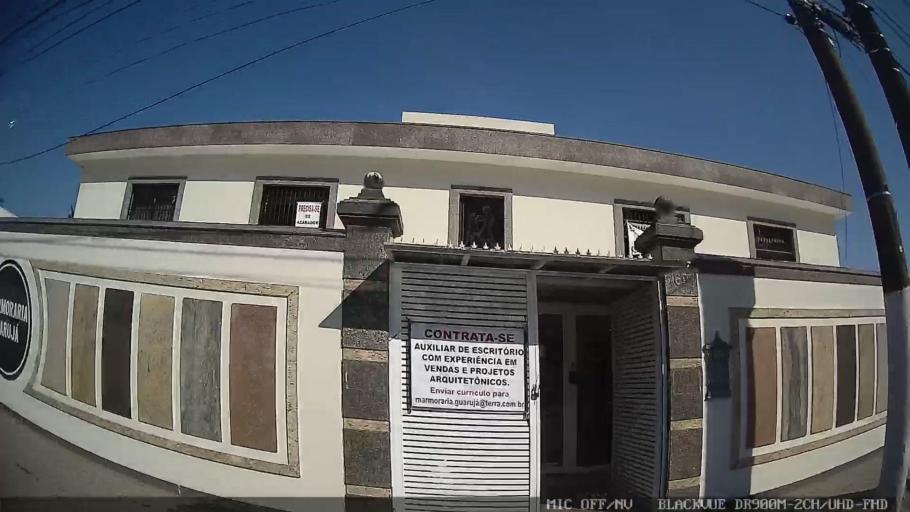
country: BR
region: Sao Paulo
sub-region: Guaruja
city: Guaruja
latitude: -23.9986
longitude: -46.2773
